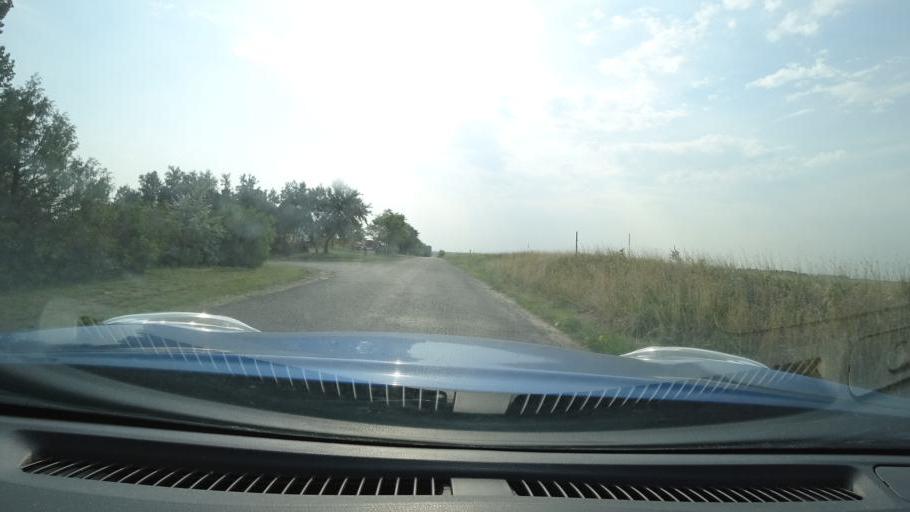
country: US
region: Colorado
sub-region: Adams County
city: Aurora
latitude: 39.7328
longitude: -104.7356
